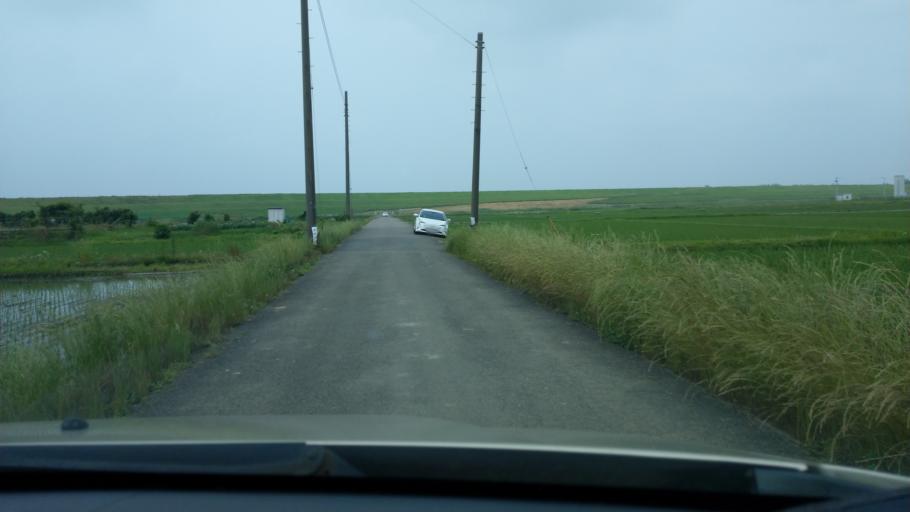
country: JP
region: Saitama
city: Yono
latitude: 35.8825
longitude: 139.5856
